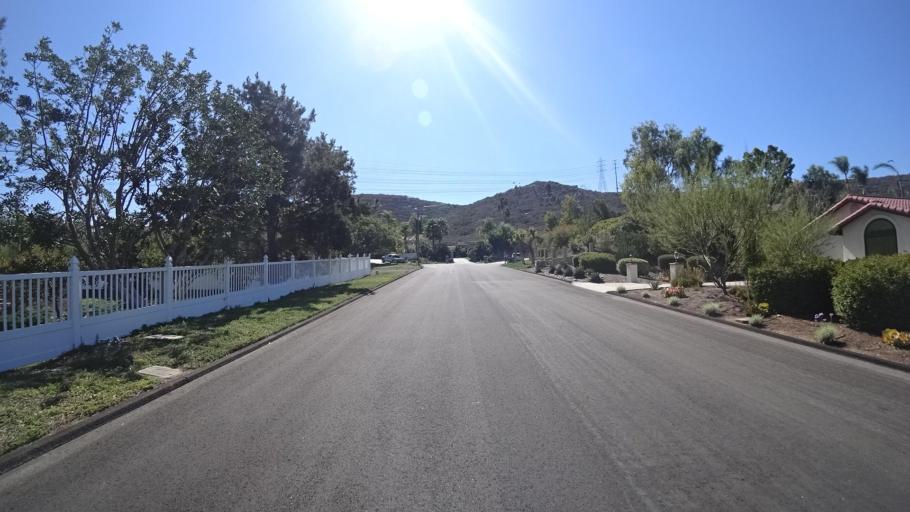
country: US
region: California
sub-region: San Diego County
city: Rancho San Diego
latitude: 32.7368
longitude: -116.9180
